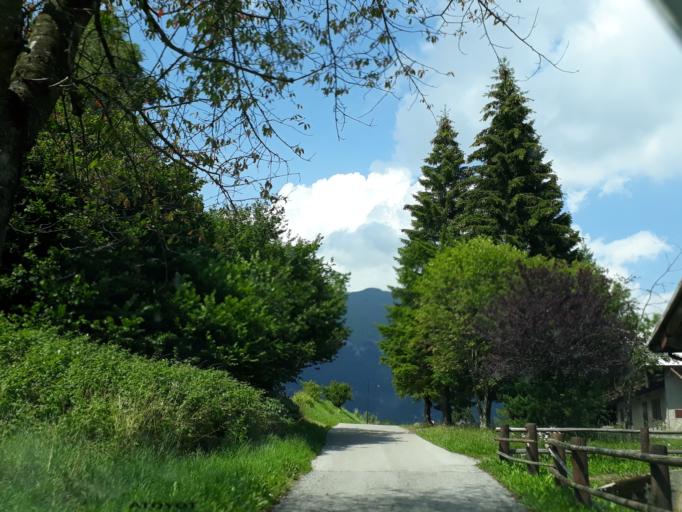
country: IT
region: Trentino-Alto Adige
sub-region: Provincia di Trento
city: Castel Condino
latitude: 45.9328
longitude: 10.6010
